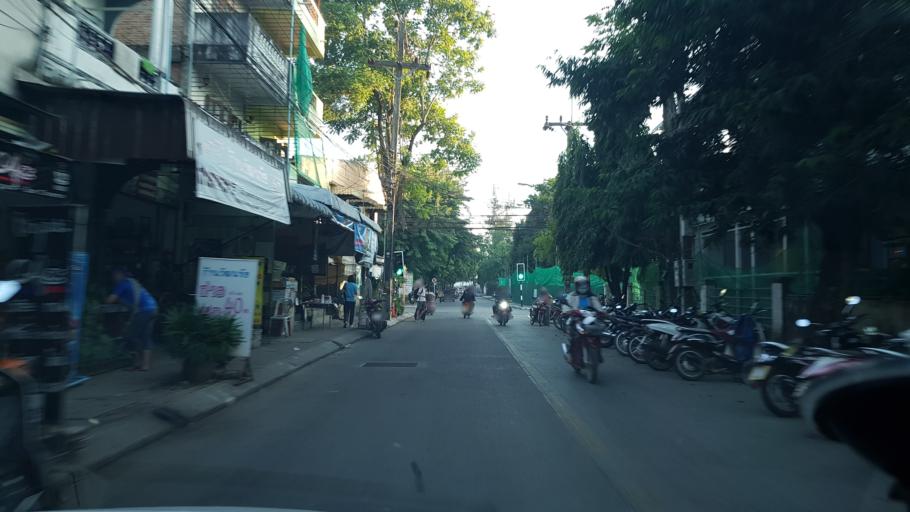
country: TH
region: Chiang Rai
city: Chiang Rai
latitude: 19.9095
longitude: 99.8351
